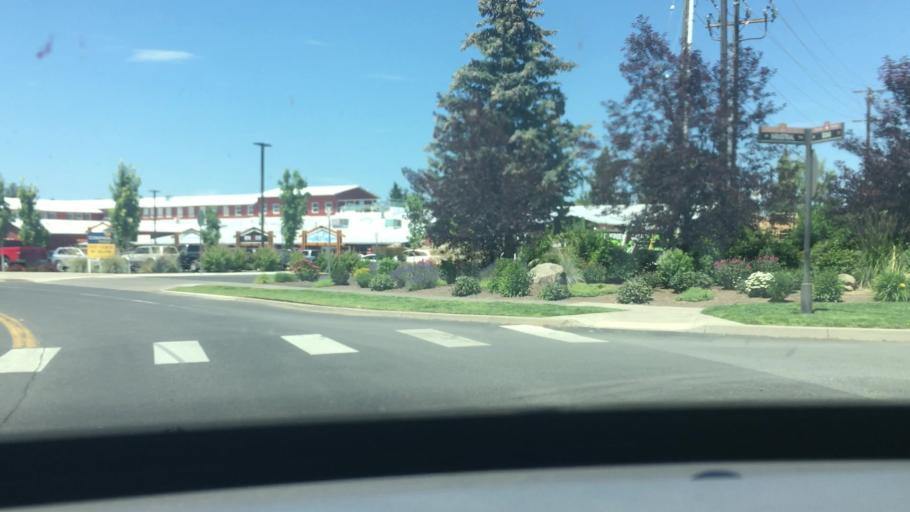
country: US
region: Oregon
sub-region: Deschutes County
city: Bend
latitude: 44.0502
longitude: -121.3140
